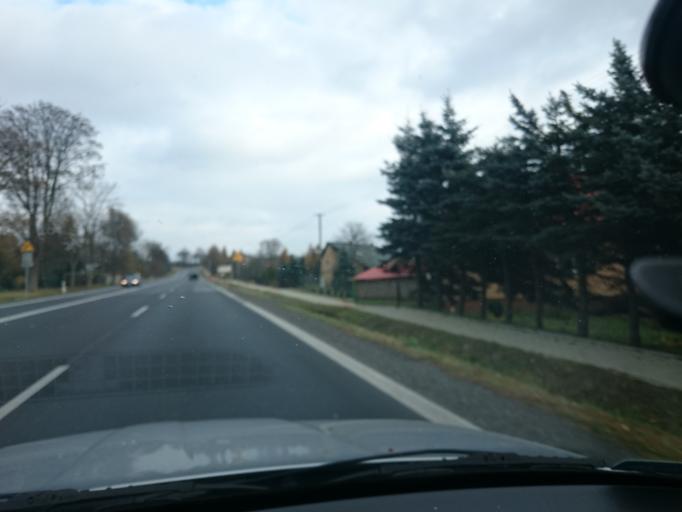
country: PL
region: Lesser Poland Voivodeship
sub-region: Powiat krakowski
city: Michalowice
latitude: 50.1767
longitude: 19.9886
